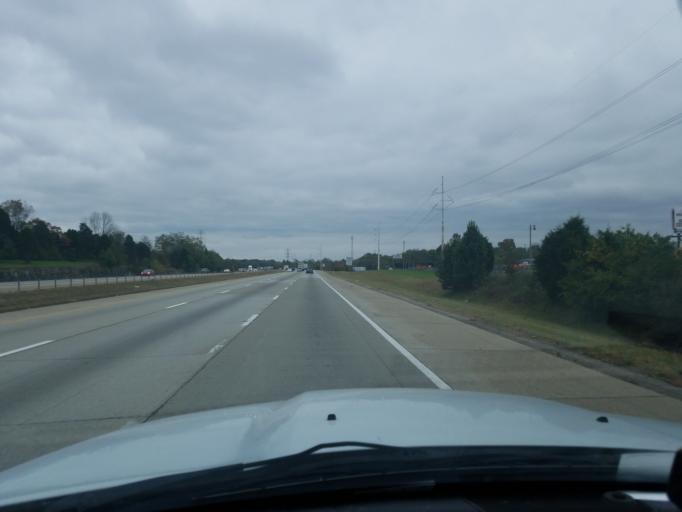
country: US
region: Kentucky
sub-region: Bullitt County
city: Brooks
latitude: 38.0518
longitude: -85.6986
